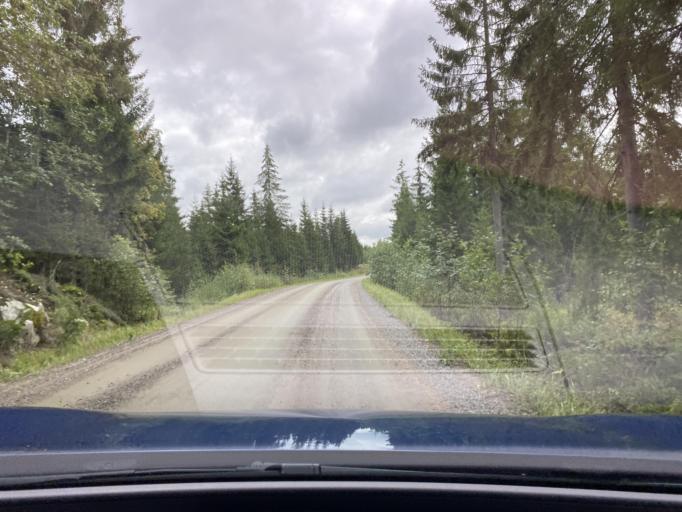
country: FI
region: Pirkanmaa
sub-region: Lounais-Pirkanmaa
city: Punkalaidun
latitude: 61.2086
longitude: 23.1776
